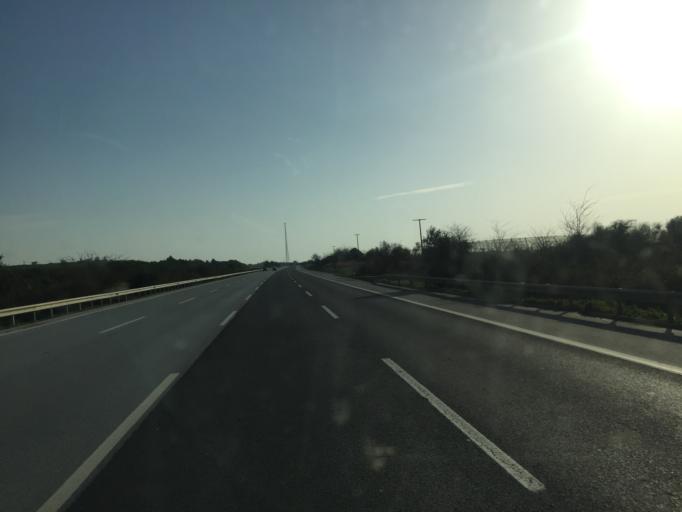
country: TR
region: Mersin
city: Yenice
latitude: 37.0233
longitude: 35.0730
